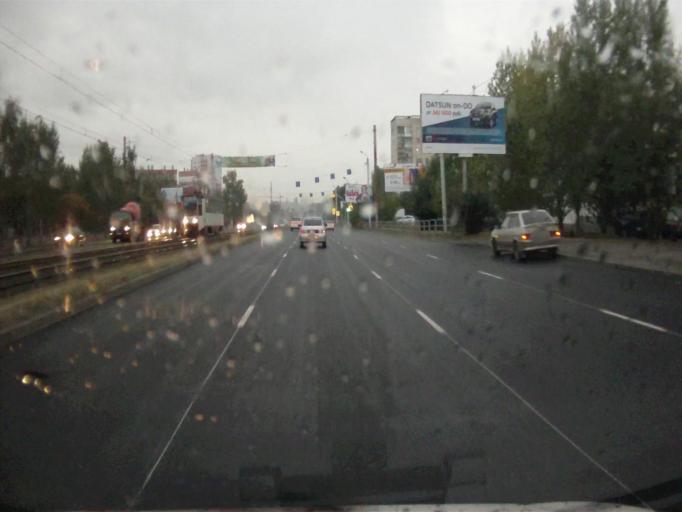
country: RU
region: Chelyabinsk
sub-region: Gorod Chelyabinsk
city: Chelyabinsk
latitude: 55.1839
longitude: 61.3827
